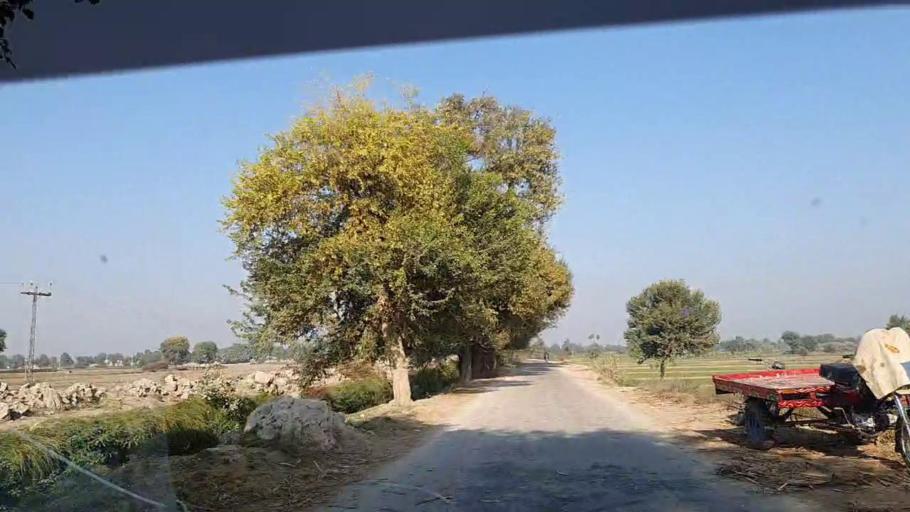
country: PK
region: Sindh
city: Sobhadero
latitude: 27.2493
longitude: 68.3277
